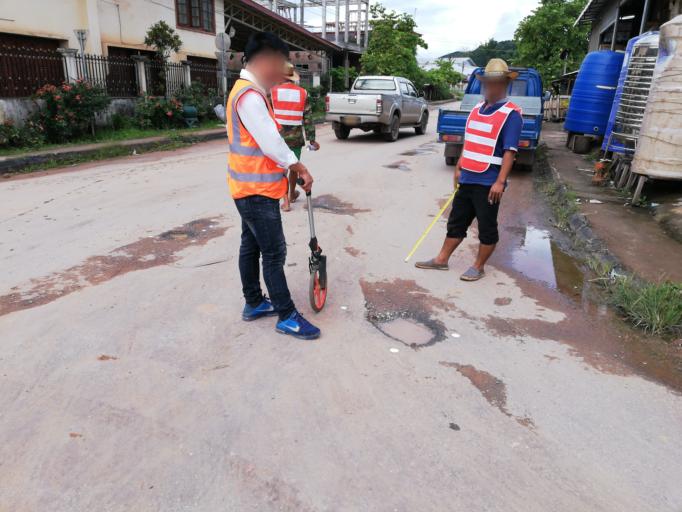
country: LA
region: Loungnamtha
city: Louang Namtha
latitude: 20.9989
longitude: 101.4050
